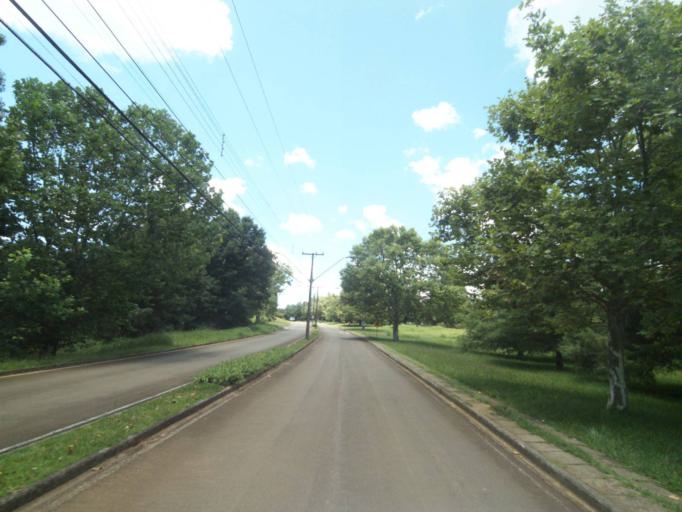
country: BR
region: Parana
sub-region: Pinhao
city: Pinhao
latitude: -25.7925
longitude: -52.0861
